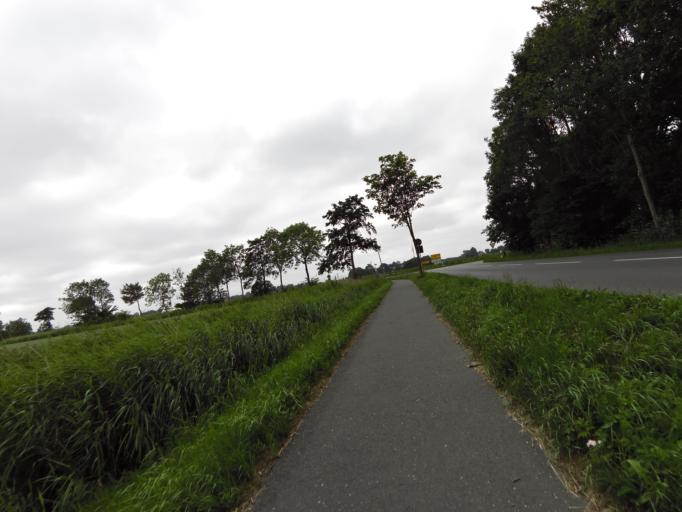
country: DE
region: Lower Saxony
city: Padingbuttel
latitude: 53.7186
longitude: 8.5452
